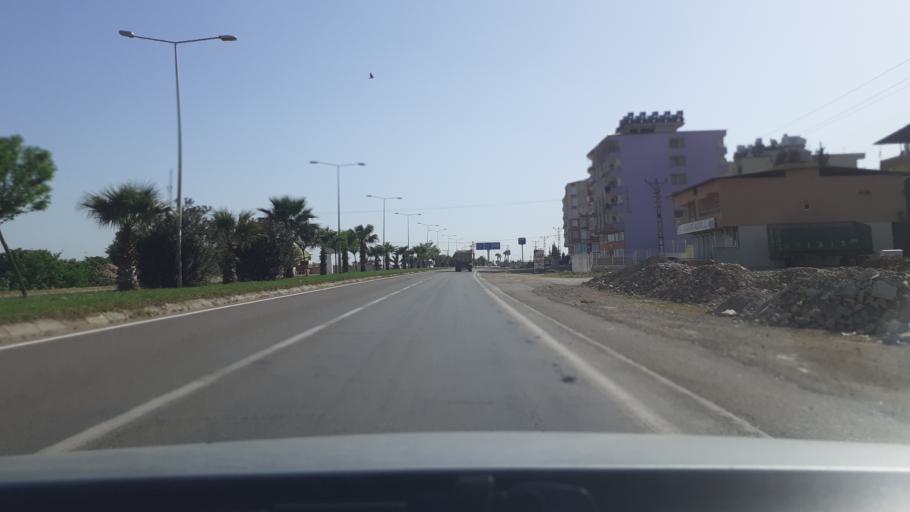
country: TR
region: Hatay
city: Kirikhan
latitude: 36.4910
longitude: 36.3695
